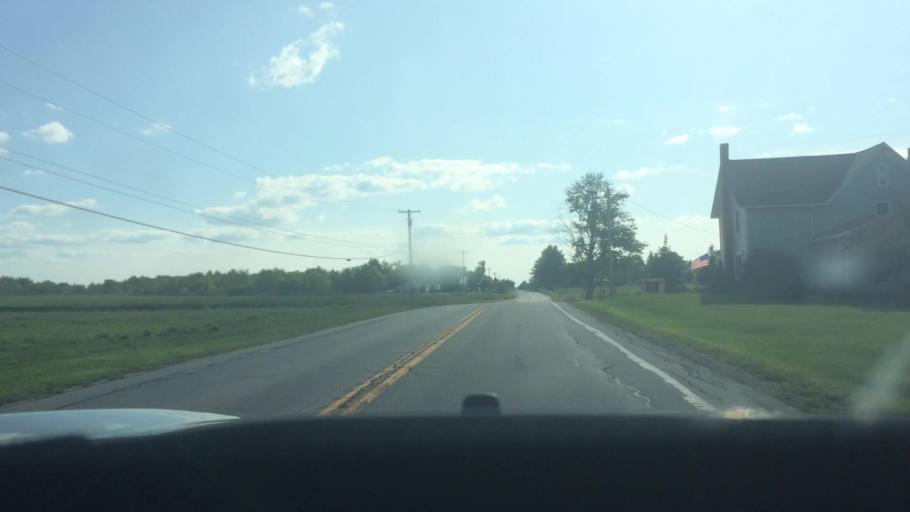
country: US
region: New York
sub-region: Franklin County
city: Malone
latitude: 44.7853
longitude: -74.4850
